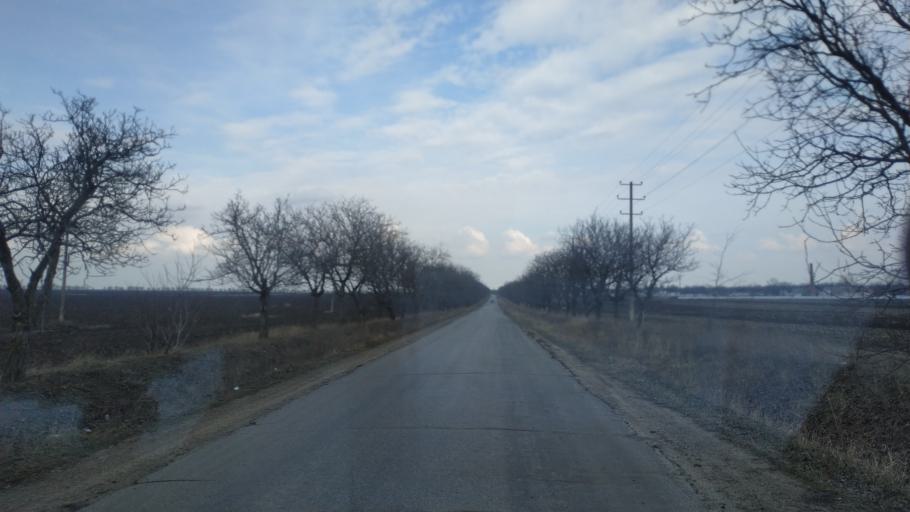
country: MD
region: Anenii Noi
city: Anenii Noi
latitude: 46.9105
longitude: 29.3262
